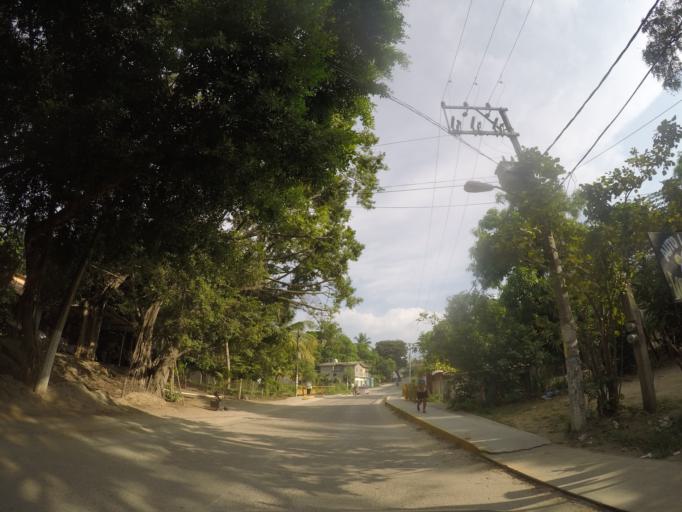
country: MX
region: Oaxaca
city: San Pedro Pochutla
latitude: 15.7528
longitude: -96.4646
